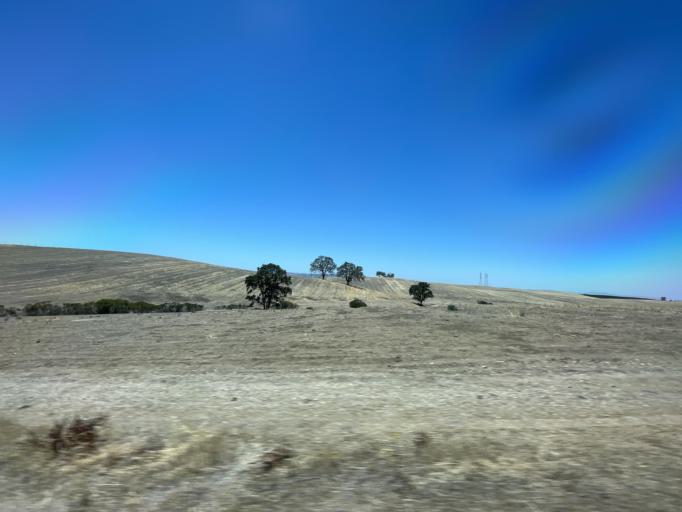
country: US
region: California
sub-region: San Luis Obispo County
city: Paso Robles
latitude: 35.6463
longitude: -120.5788
